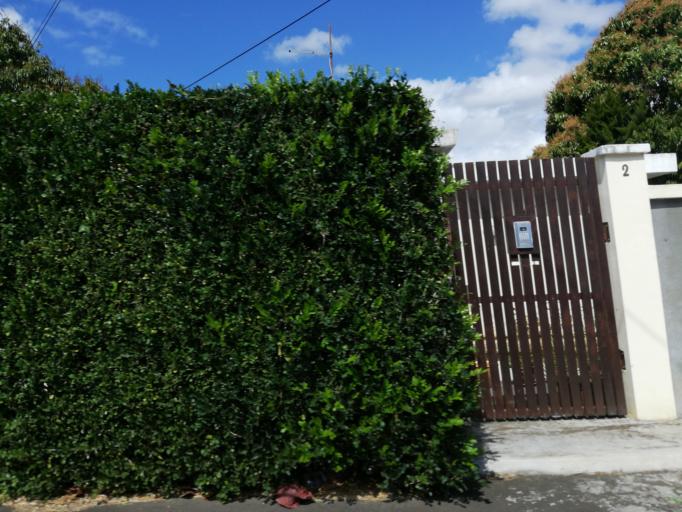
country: MU
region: Plaines Wilhems
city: Ebene
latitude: -20.2337
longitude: 57.4645
